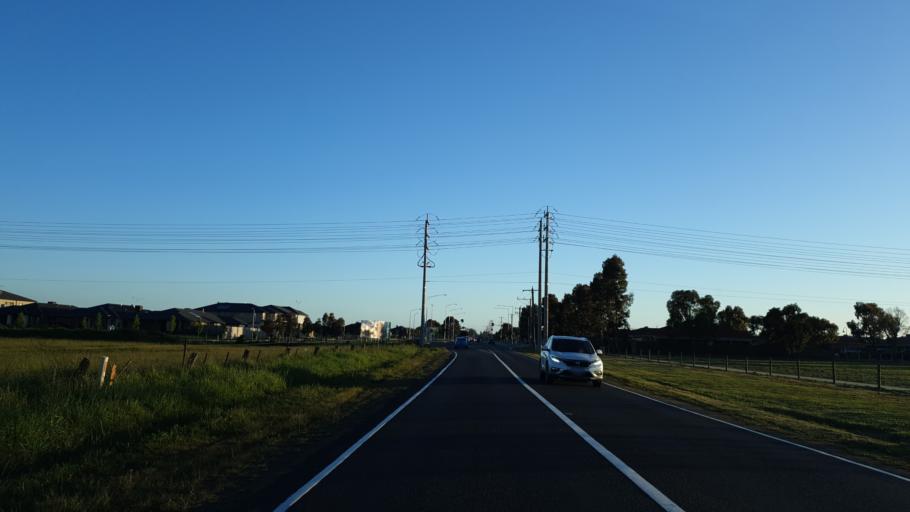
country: AU
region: Victoria
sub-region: Casey
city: Cranbourne
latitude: -38.0907
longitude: 145.2942
